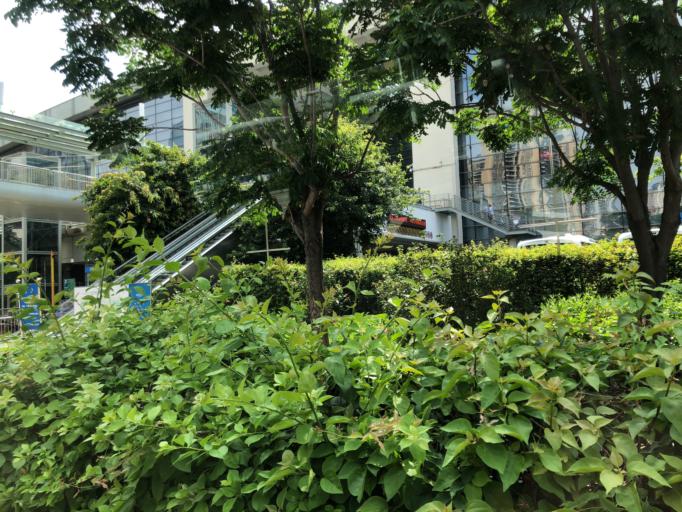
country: CN
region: Guangdong
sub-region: Shenzhen
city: Shenzhen
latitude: 22.5331
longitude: 114.0516
